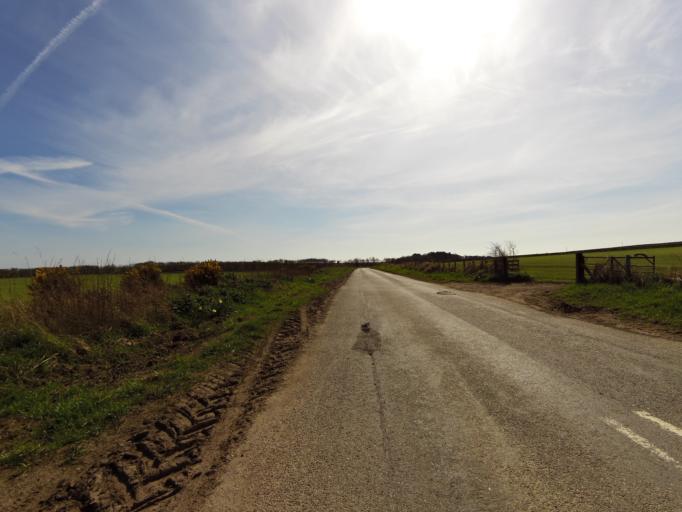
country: GB
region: Scotland
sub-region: Angus
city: Arbroath
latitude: 56.5845
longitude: -2.5554
